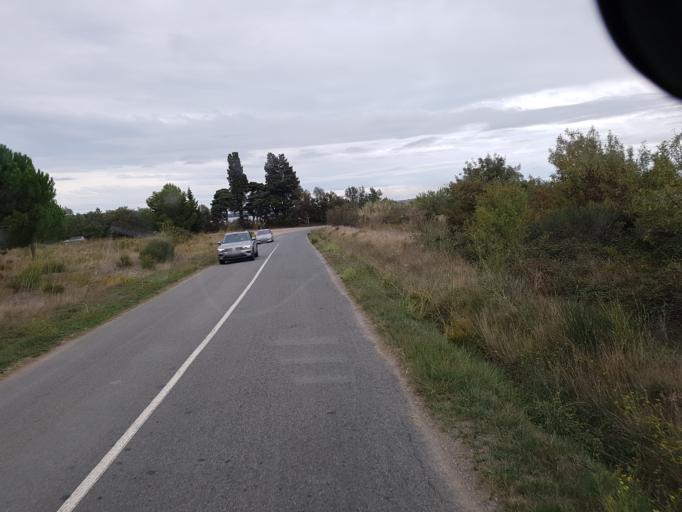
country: FR
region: Languedoc-Roussillon
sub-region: Departement de l'Aude
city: Narbonne
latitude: 43.1445
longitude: 2.9824
